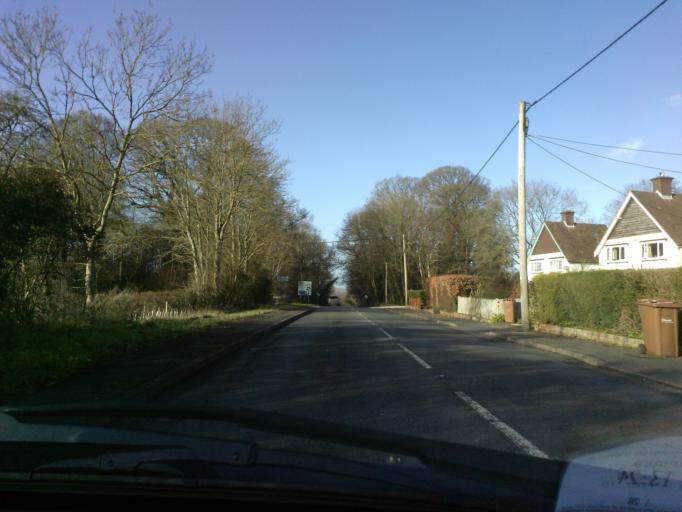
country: GB
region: England
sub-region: Hampshire
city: Totton
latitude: 50.9522
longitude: -1.4688
